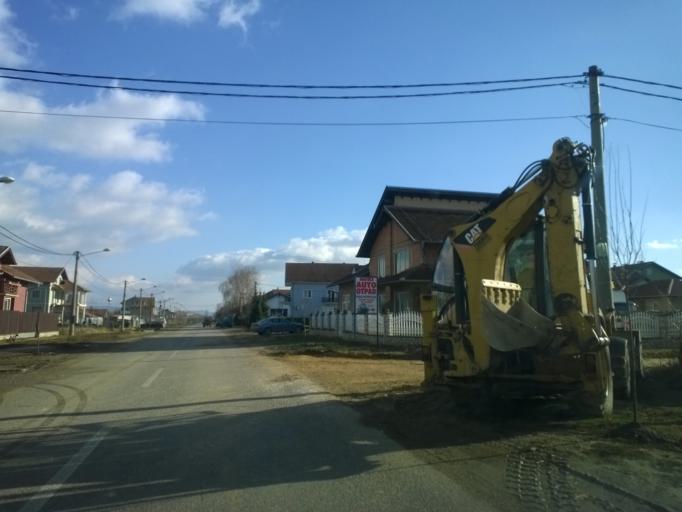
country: RS
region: Central Serbia
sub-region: Branicevski Okrug
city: Veliko Gradiste
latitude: 44.7570
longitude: 21.5073
